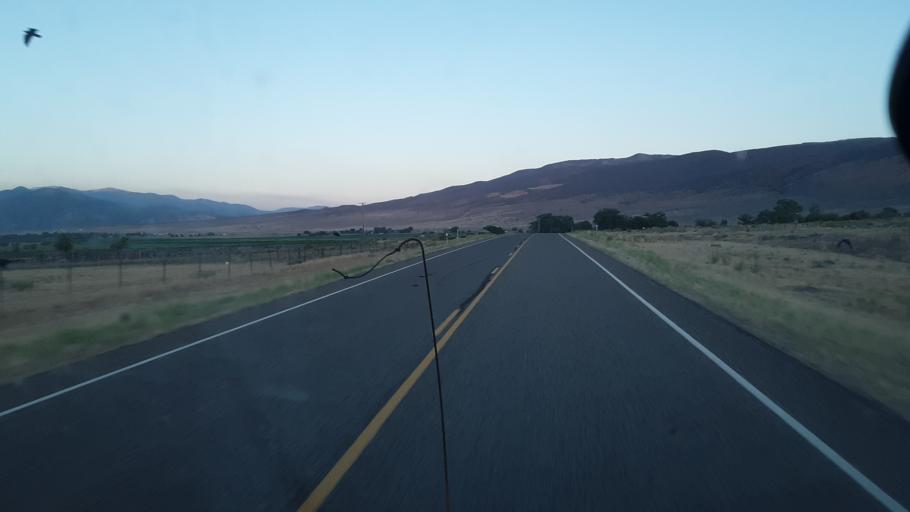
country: US
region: Utah
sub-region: Sevier County
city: Monroe
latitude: 38.6551
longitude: -112.1888
